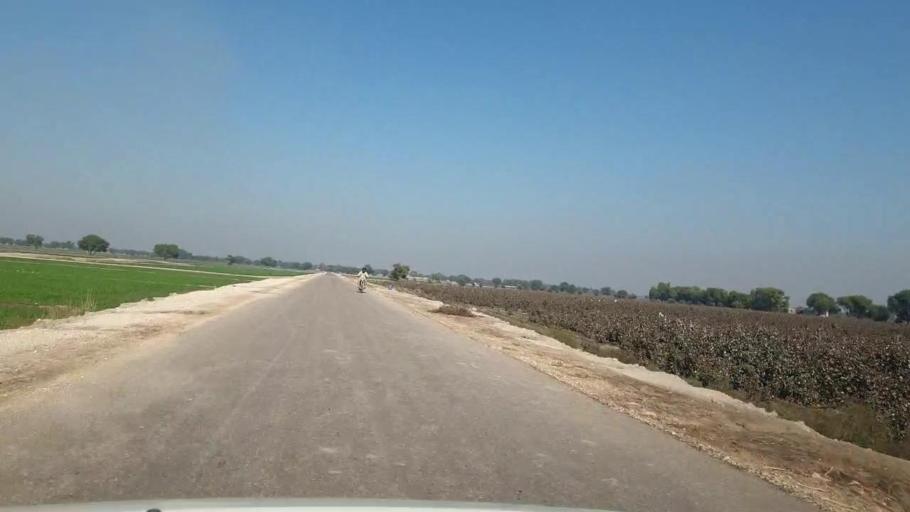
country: PK
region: Sindh
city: Bhan
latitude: 26.6563
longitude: 67.7061
